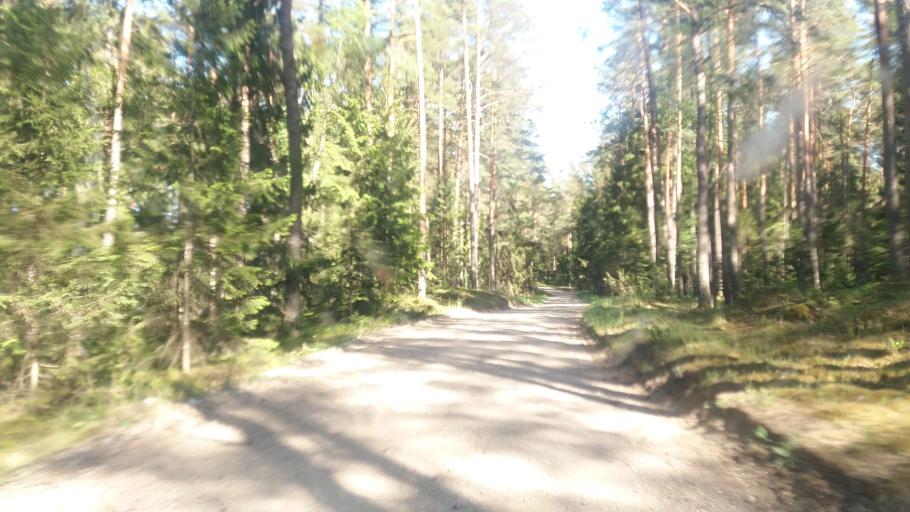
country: LV
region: Kuldigas Rajons
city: Kuldiga
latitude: 57.0796
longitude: 21.8023
